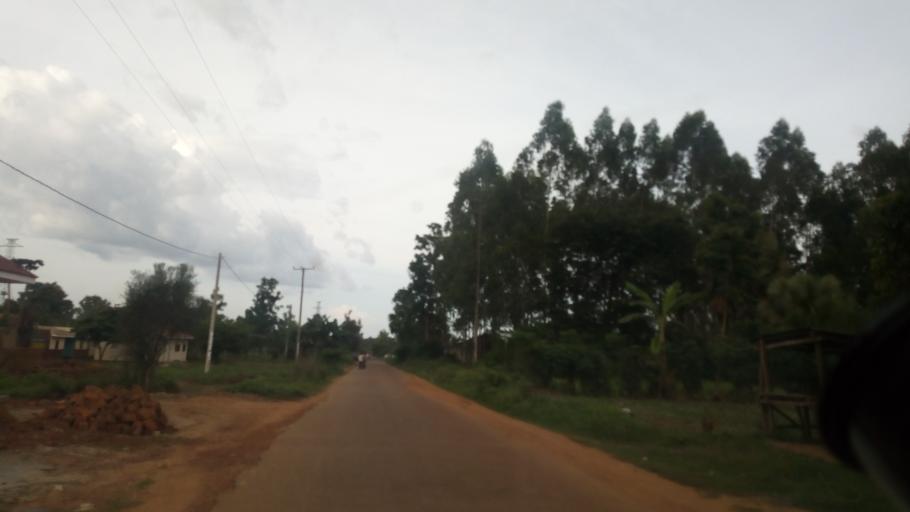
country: UG
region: Northern Region
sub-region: Lira District
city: Lira
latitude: 2.2619
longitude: 32.8604
